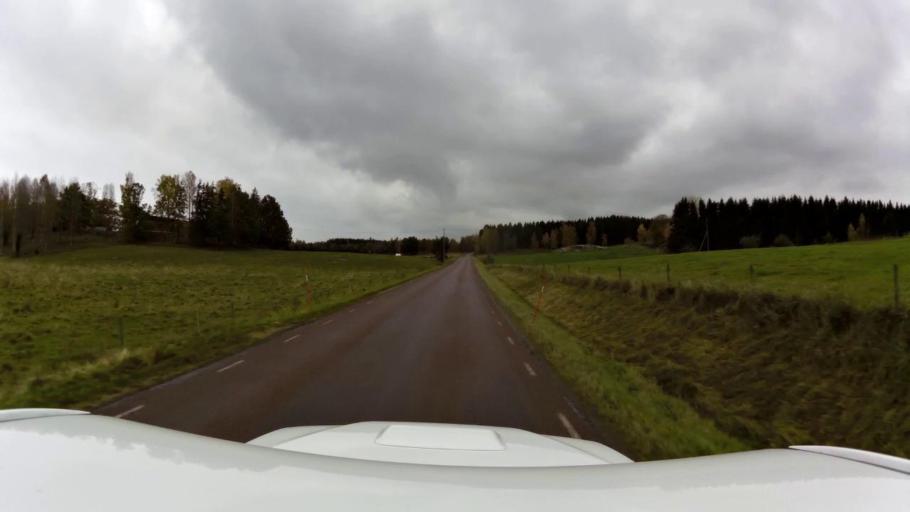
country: SE
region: OEstergoetland
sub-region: Linkopings Kommun
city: Ljungsbro
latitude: 58.5433
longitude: 15.5259
